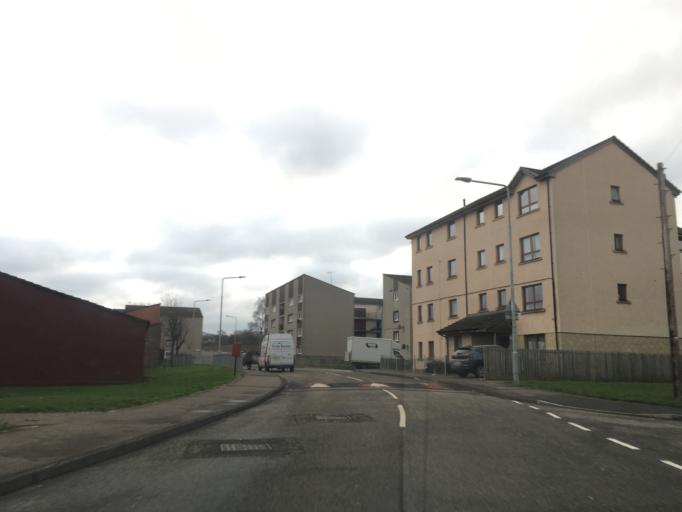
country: GB
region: Scotland
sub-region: Edinburgh
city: Currie
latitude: 55.9197
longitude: -3.2910
